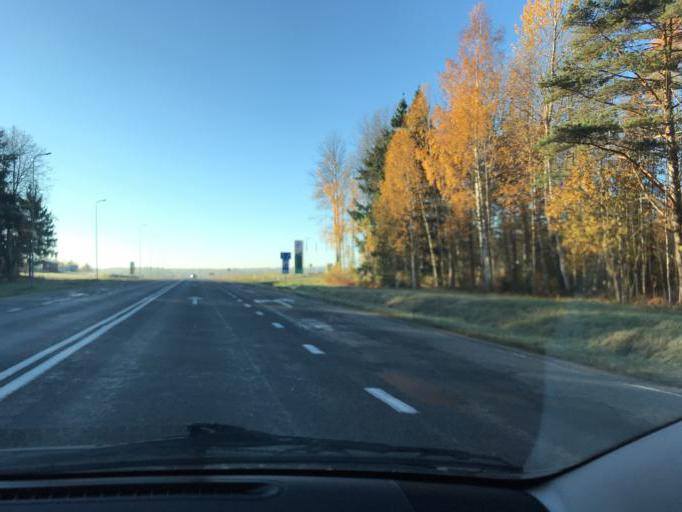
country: BY
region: Vitebsk
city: Vitebsk
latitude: 54.9123
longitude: 30.3756
